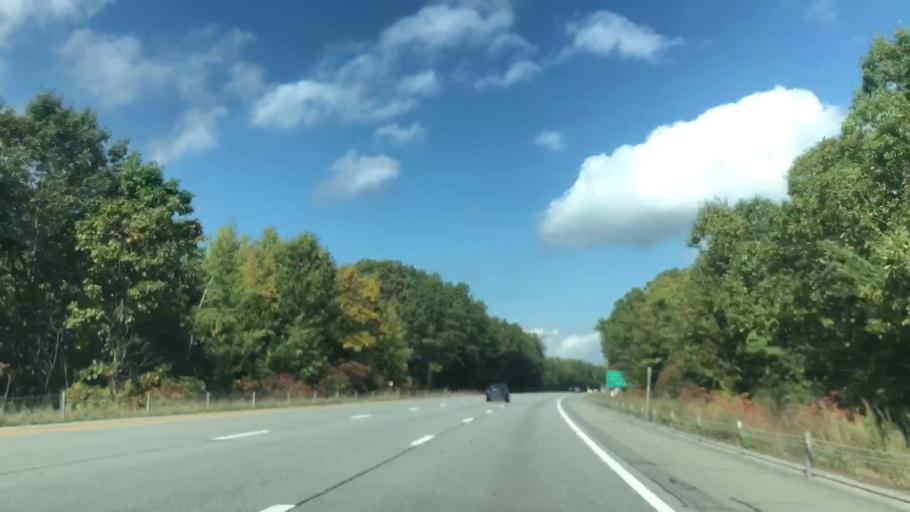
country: US
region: New York
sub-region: Warren County
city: West Glens Falls
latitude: 43.2829
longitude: -73.6800
